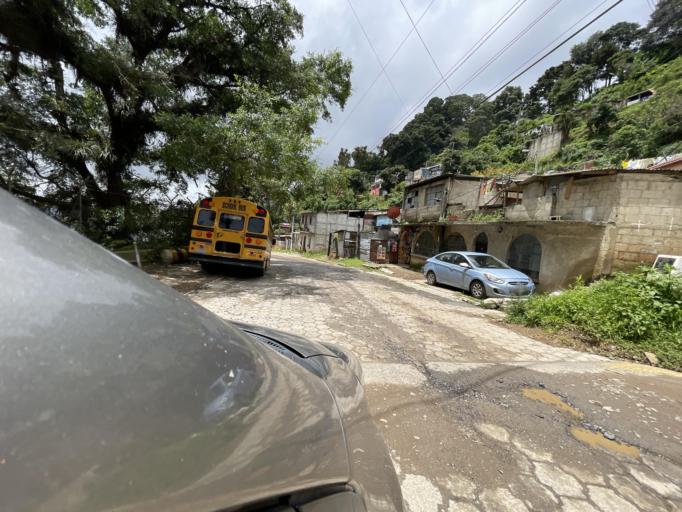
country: GT
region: Guatemala
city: Mixco
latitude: 14.6393
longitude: -90.6239
